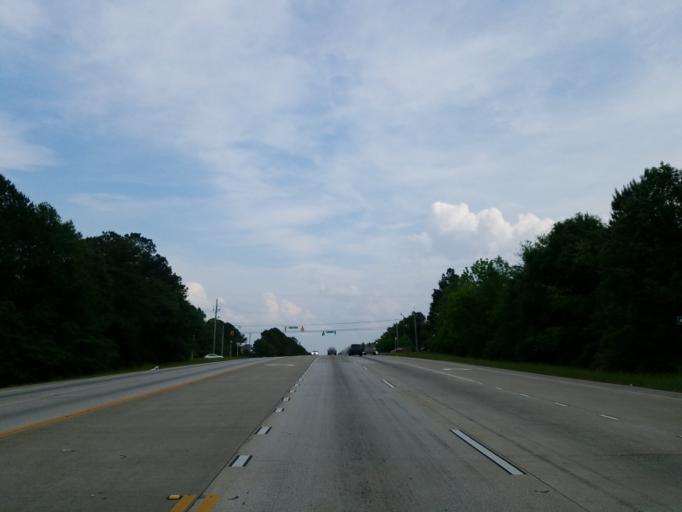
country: US
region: Georgia
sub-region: Cobb County
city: Powder Springs
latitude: 33.8497
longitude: -84.6954
